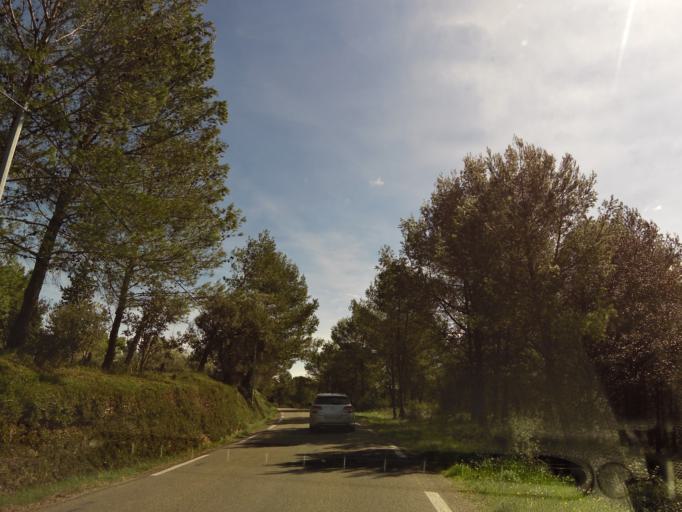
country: FR
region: Languedoc-Roussillon
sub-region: Departement du Gard
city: Bernis
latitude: 43.7795
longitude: 4.2756
